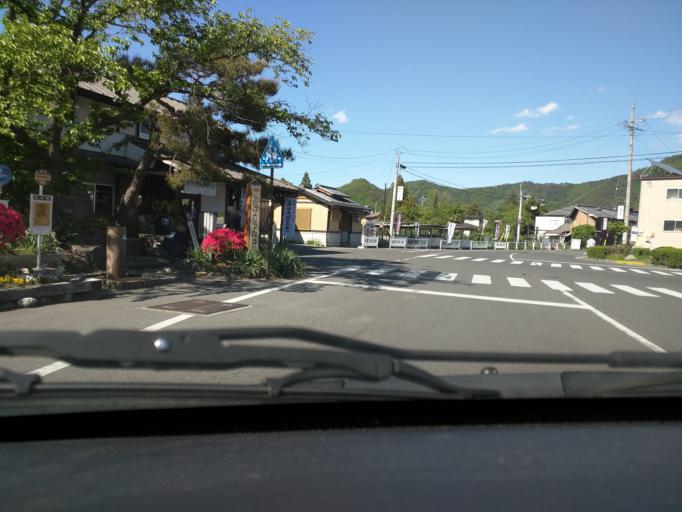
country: JP
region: Nagano
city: Nagano-shi
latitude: 36.5657
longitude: 138.1983
